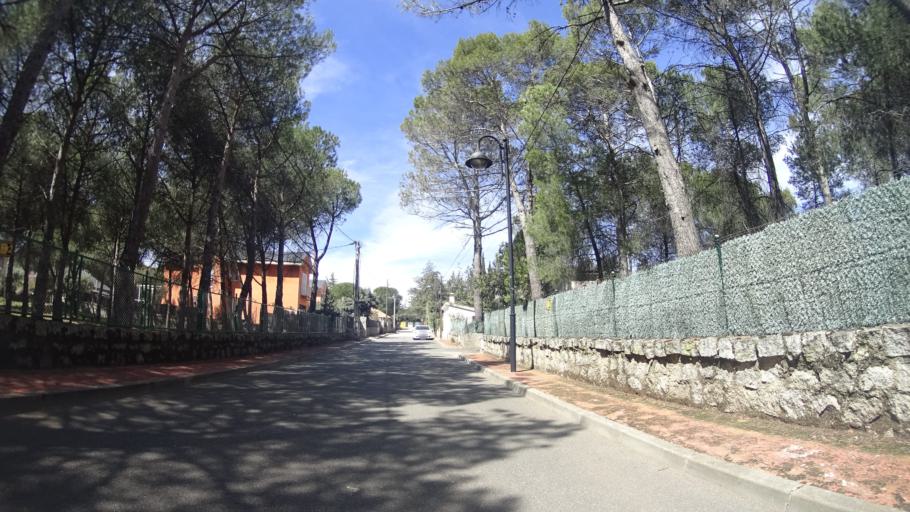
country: ES
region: Madrid
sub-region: Provincia de Madrid
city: Galapagar
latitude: 40.5891
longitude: -3.9873
